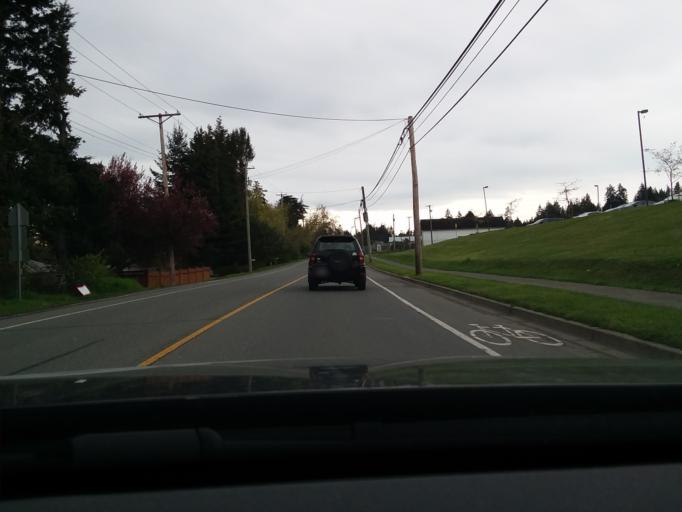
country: CA
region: British Columbia
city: North Saanich
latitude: 48.6242
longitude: -123.4184
